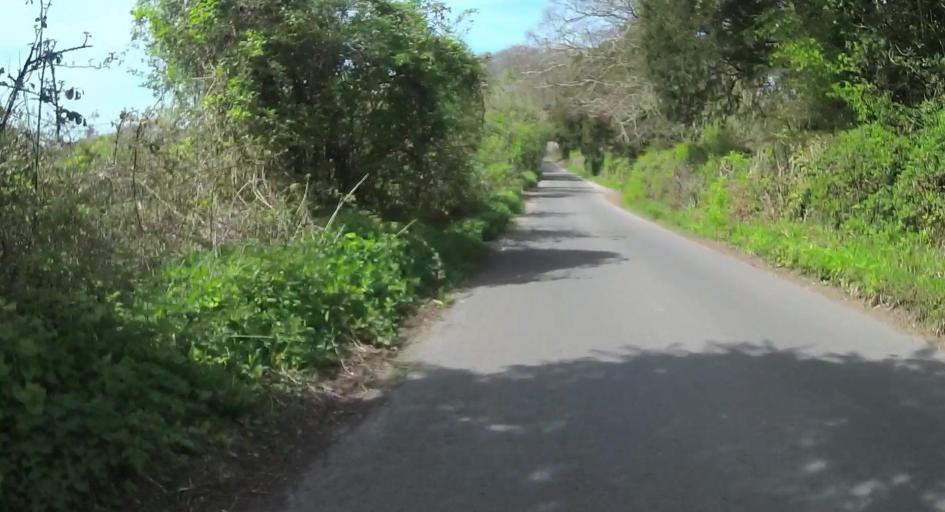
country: GB
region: England
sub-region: Hampshire
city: Chandlers Ford
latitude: 51.0601
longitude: -1.3712
